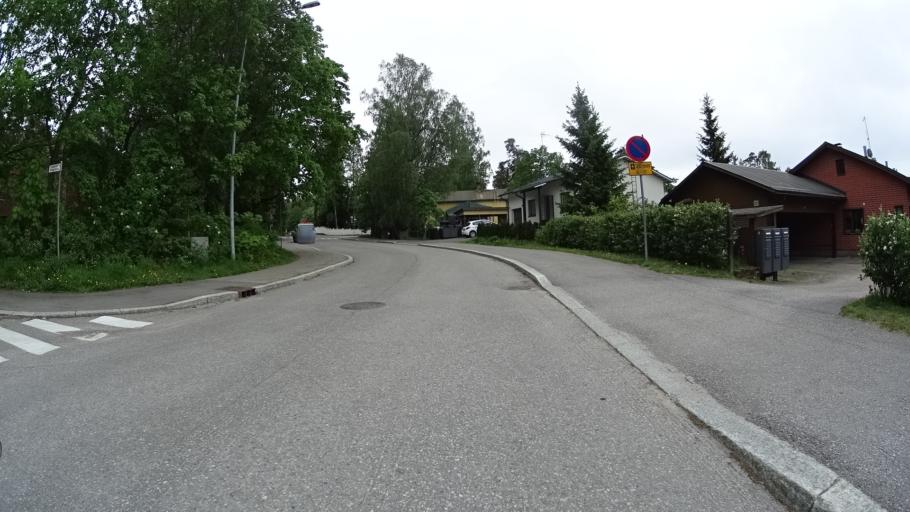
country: FI
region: Uusimaa
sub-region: Helsinki
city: Vantaa
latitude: 60.2666
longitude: 25.0646
